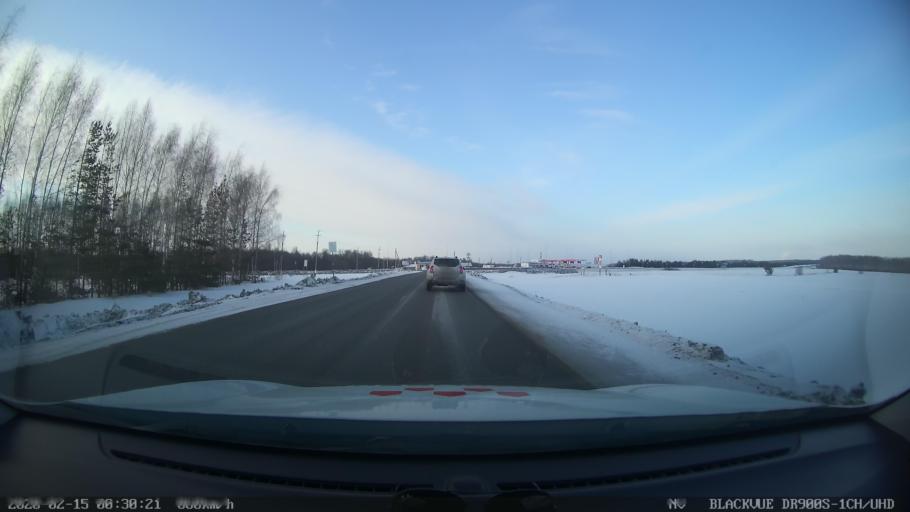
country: RU
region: Tatarstan
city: Verkhniy Uslon
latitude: 55.6582
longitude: 48.8588
